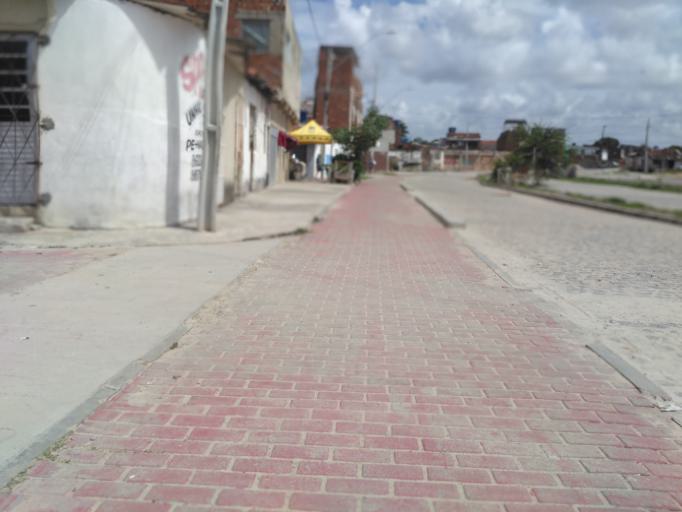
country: BR
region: Pernambuco
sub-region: Recife
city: Recife
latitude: -8.0727
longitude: -34.8994
